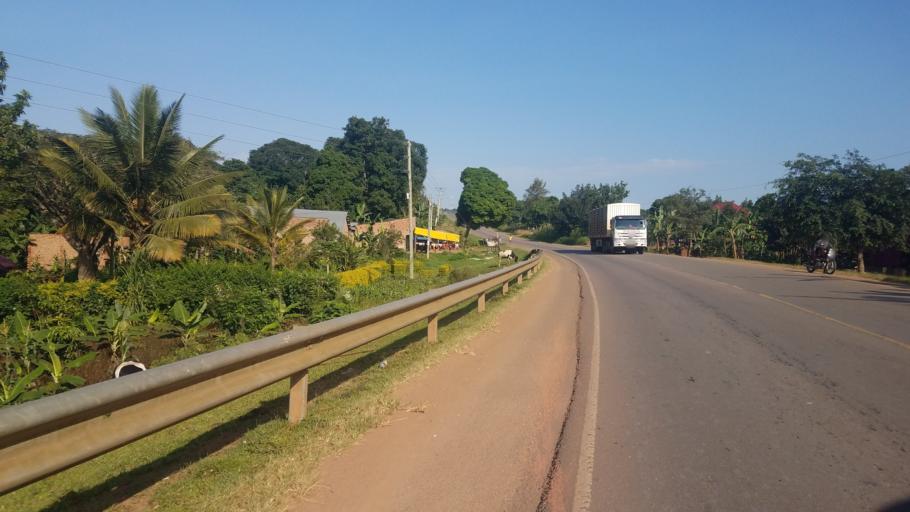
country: UG
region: Central Region
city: Masaka
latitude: -0.3367
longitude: 31.6968
